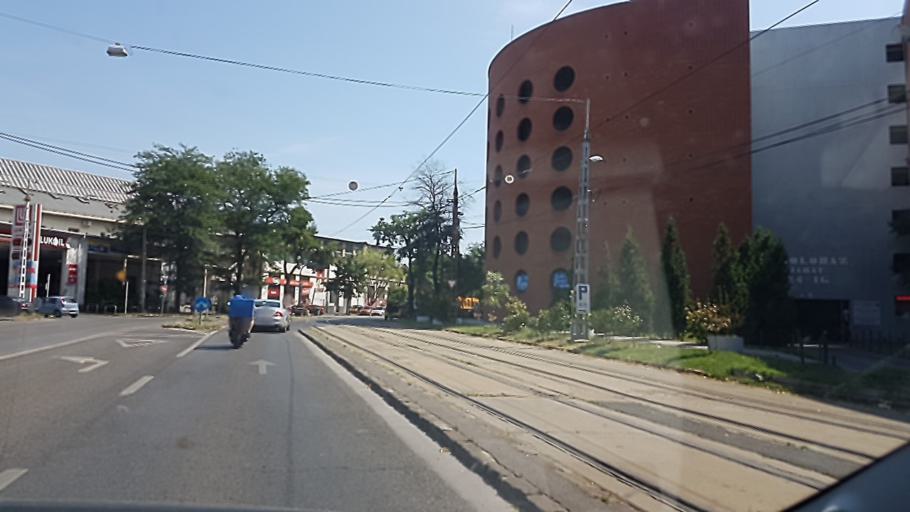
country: HU
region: Budapest
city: Budapest VIII. keruelet
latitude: 47.4888
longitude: 19.0919
